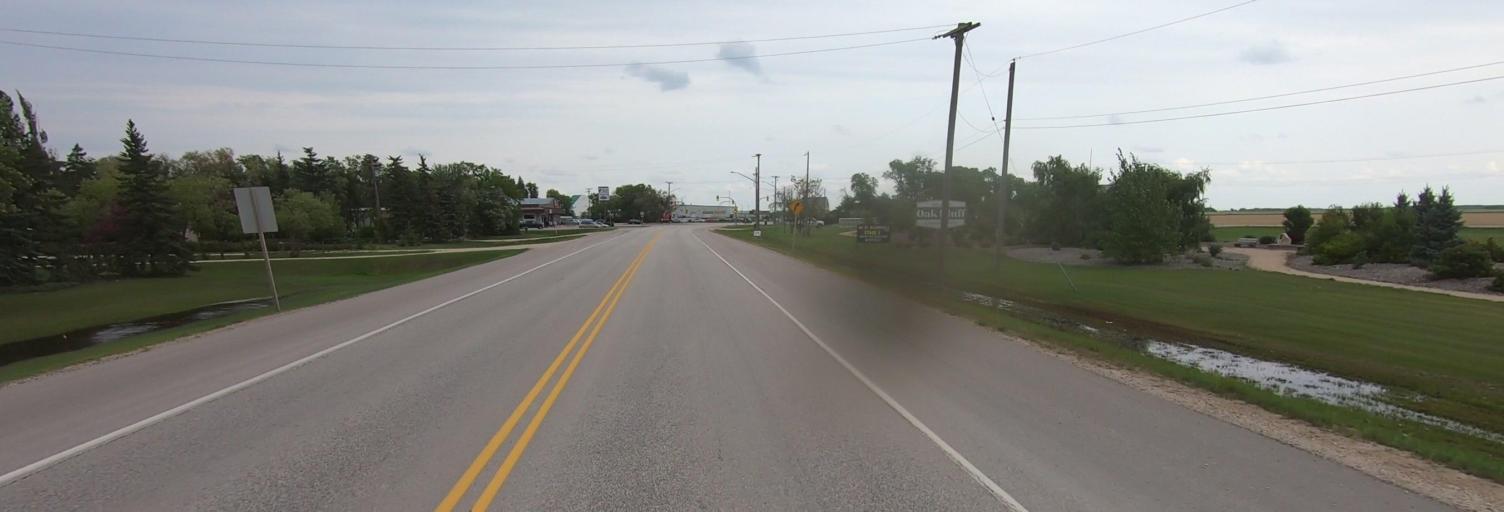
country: CA
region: Manitoba
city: Headingley
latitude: 49.7721
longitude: -97.3244
